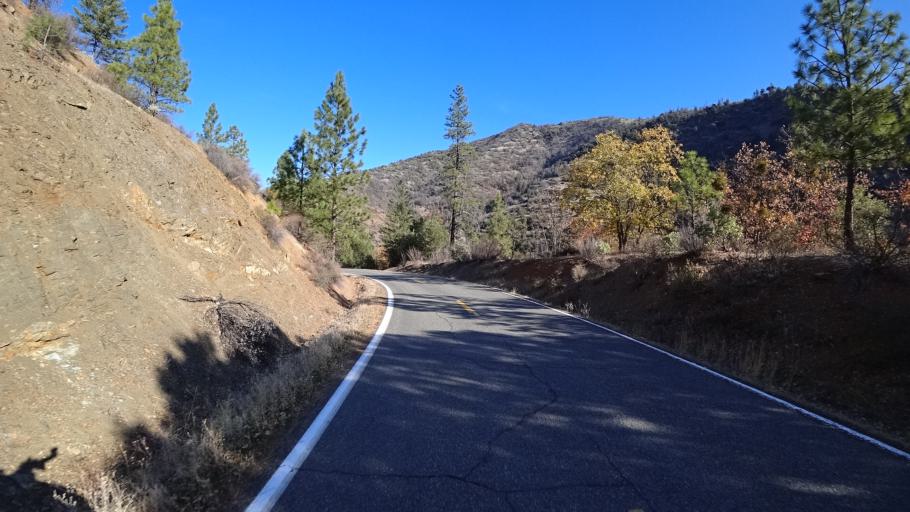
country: US
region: California
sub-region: Siskiyou County
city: Yreka
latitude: 41.9046
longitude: -122.8299
